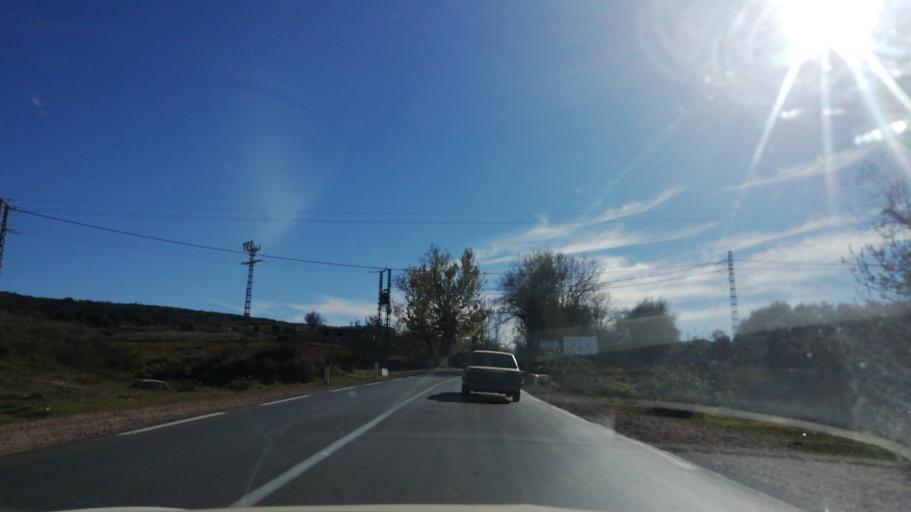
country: DZ
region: Tlemcen
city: Mansoura
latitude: 34.8367
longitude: -1.3725
